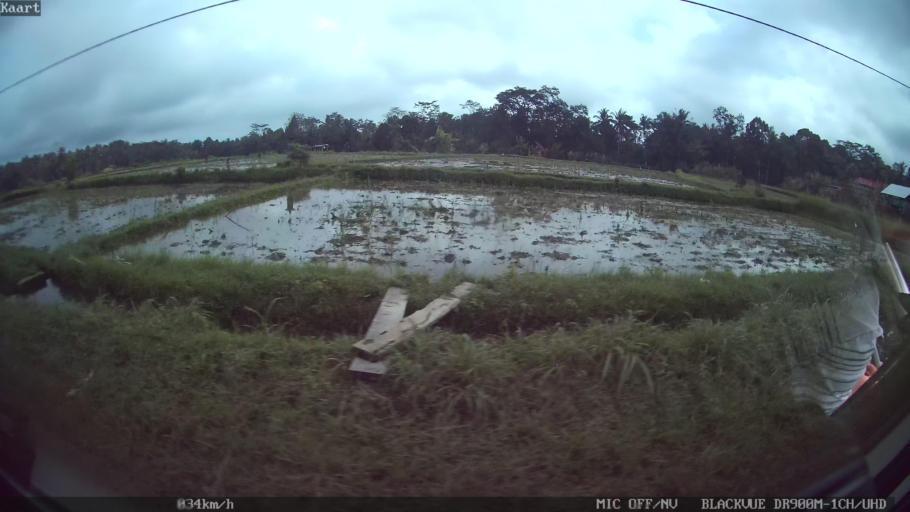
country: ID
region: Bali
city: Bunutan
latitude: -8.4649
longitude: 115.2349
